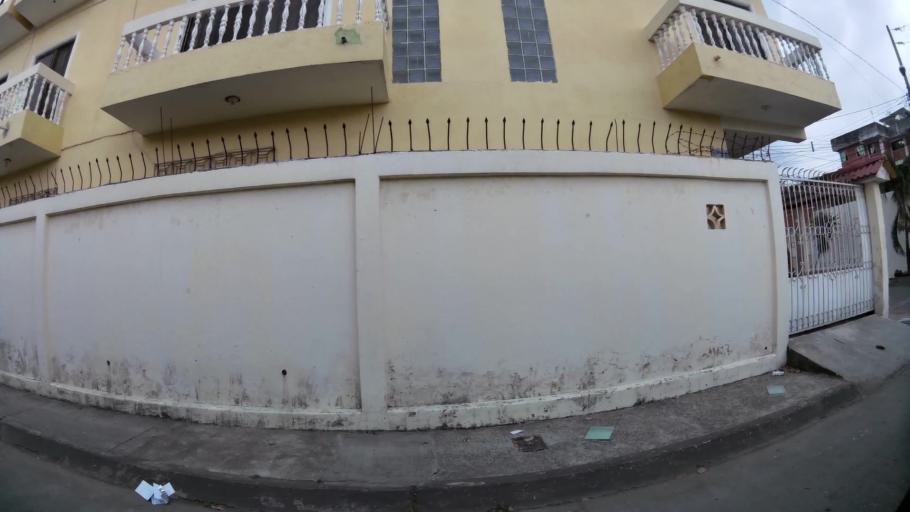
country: EC
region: Guayas
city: Eloy Alfaro
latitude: -2.1215
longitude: -79.8871
